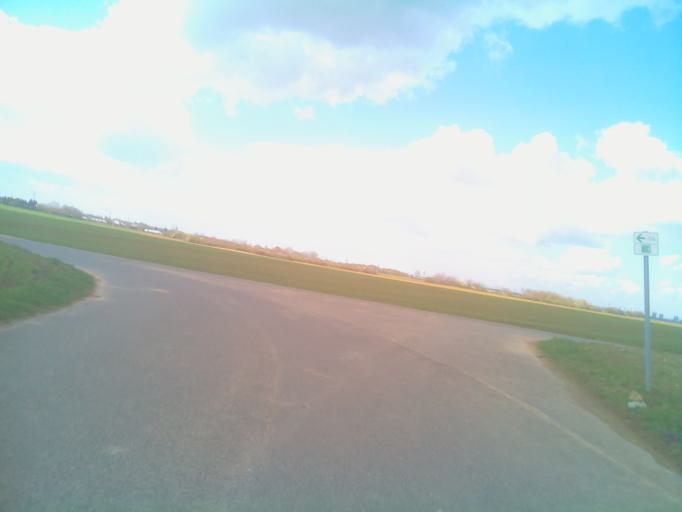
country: DE
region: Baden-Wuerttemberg
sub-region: Karlsruhe Region
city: Ladenburg
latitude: 49.4905
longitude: 8.6349
